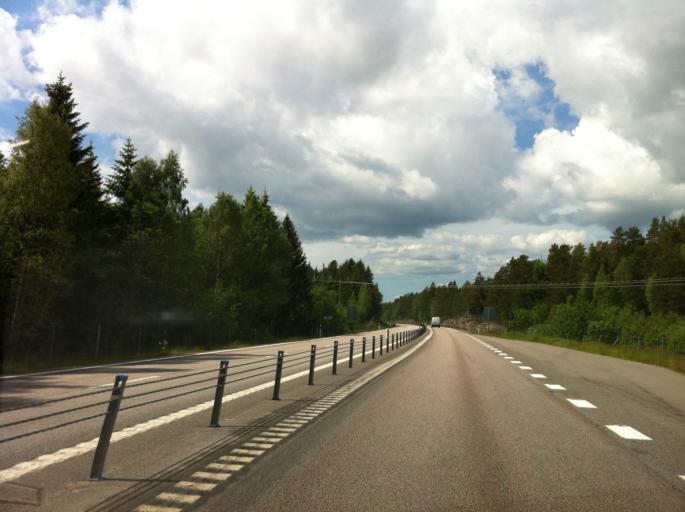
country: SE
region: Vaermland
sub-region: Saffle Kommun
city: Saeffle
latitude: 59.1269
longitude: 12.8744
